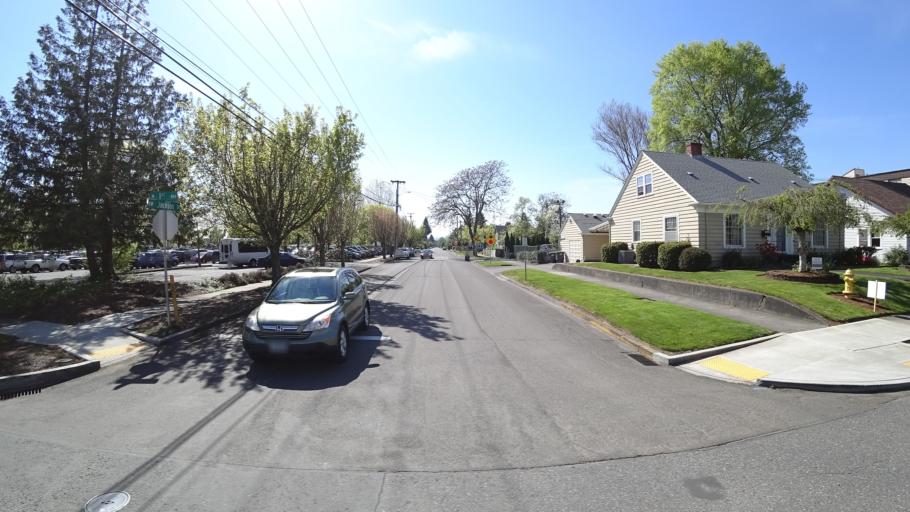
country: US
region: Oregon
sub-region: Washington County
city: Hillsboro
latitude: 45.5253
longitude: -122.9897
